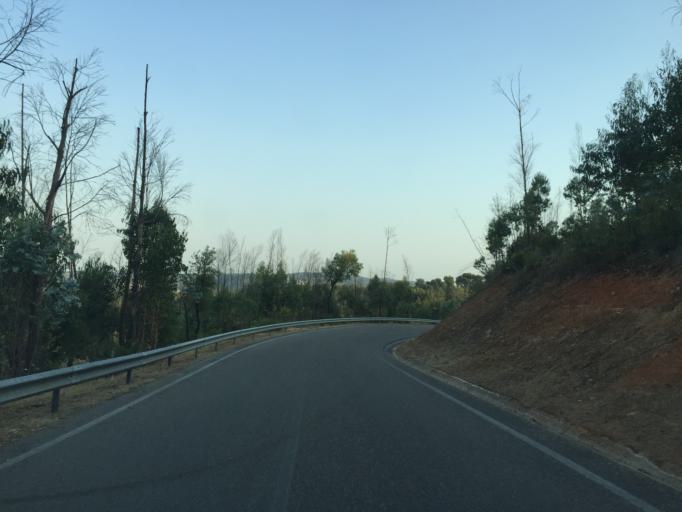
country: PT
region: Santarem
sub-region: Ferreira do Zezere
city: Ferreira do Zezere
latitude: 39.5814
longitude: -8.2967
